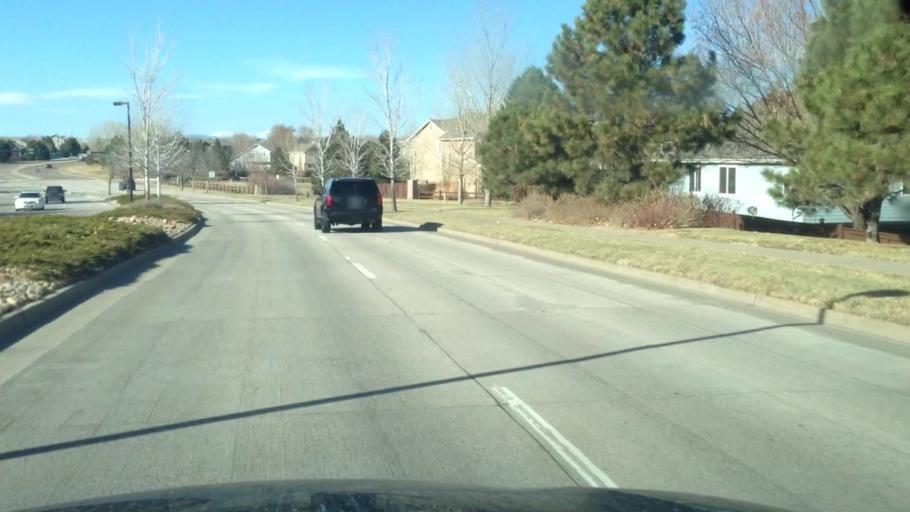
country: US
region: Colorado
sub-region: Douglas County
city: Stonegate
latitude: 39.5152
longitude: -104.7956
